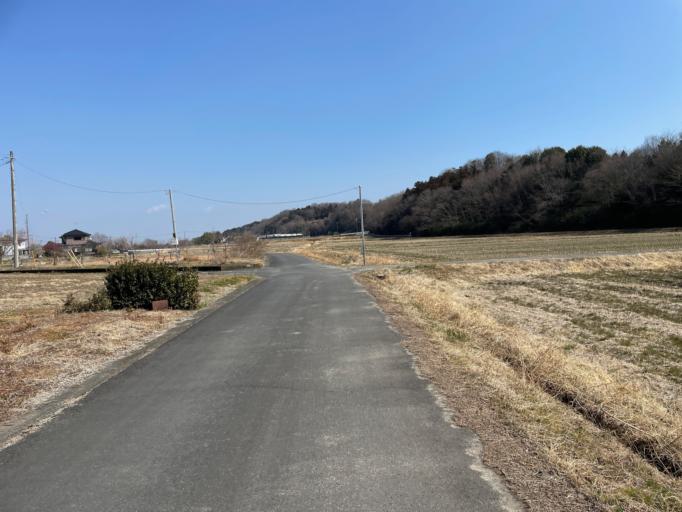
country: JP
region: Saitama
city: Yorii
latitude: 36.1138
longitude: 139.2260
